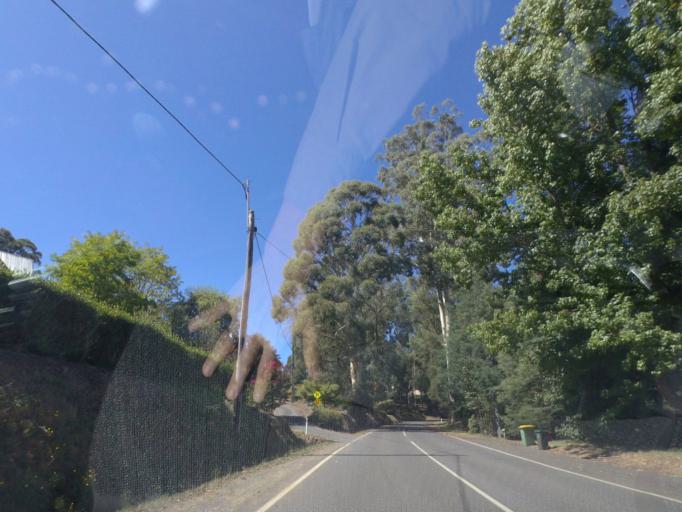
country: AU
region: Victoria
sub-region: Yarra Ranges
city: Millgrove
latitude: -37.5093
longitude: 145.7501
